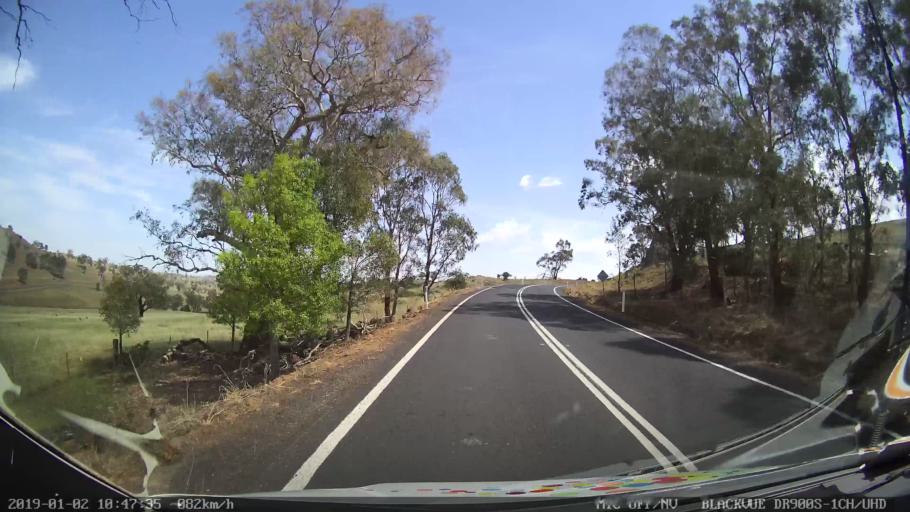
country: AU
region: New South Wales
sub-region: Cootamundra
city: Cootamundra
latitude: -34.7435
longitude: 148.2721
